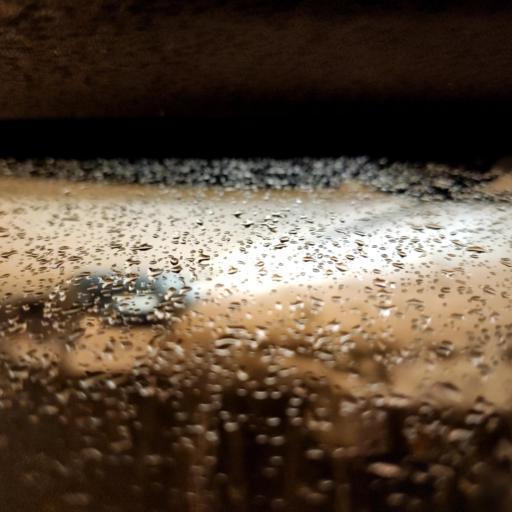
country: RU
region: Perm
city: Polazna
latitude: 58.1372
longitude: 56.3821
